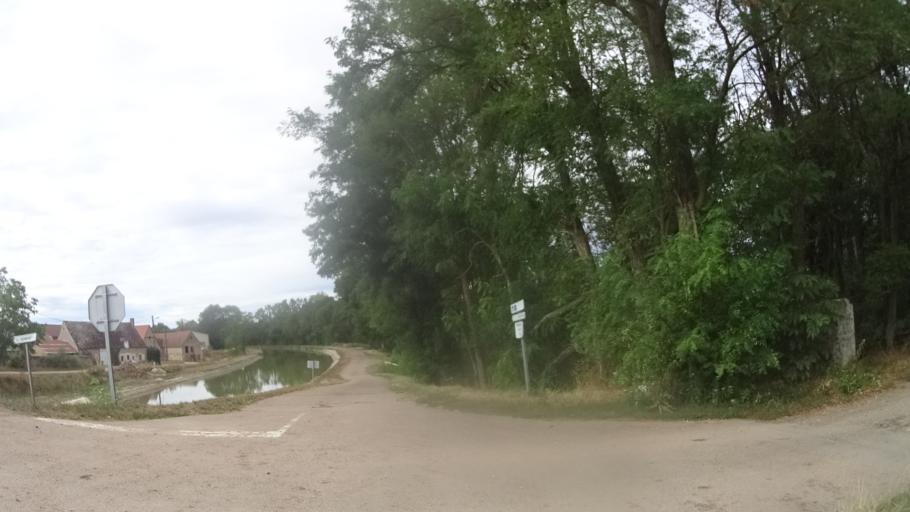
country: FR
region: Bourgogne
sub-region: Departement de la Nievre
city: Sermoise-sur-Loire
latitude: 46.9593
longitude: 3.1978
